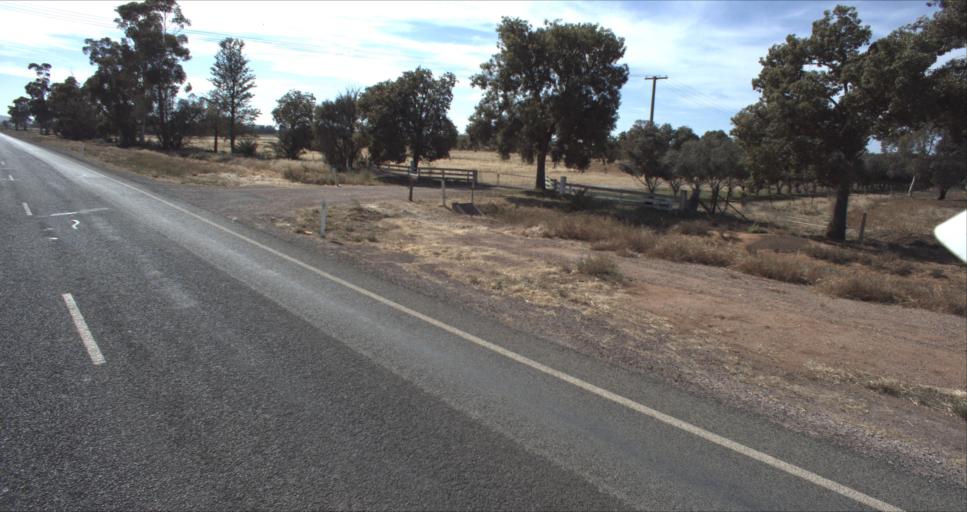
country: AU
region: New South Wales
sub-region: Leeton
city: Leeton
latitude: -34.5607
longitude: 146.4371
